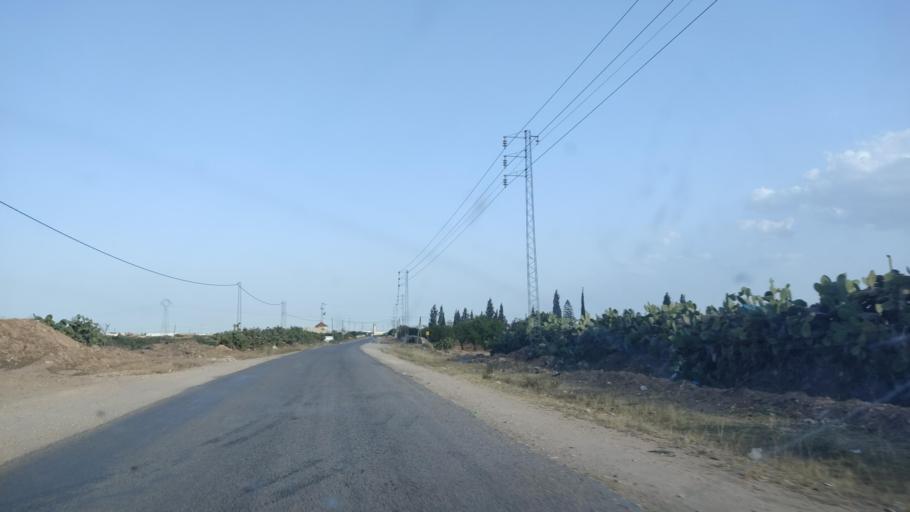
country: TN
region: Safaqis
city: Sfax
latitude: 34.8075
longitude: 10.6665
